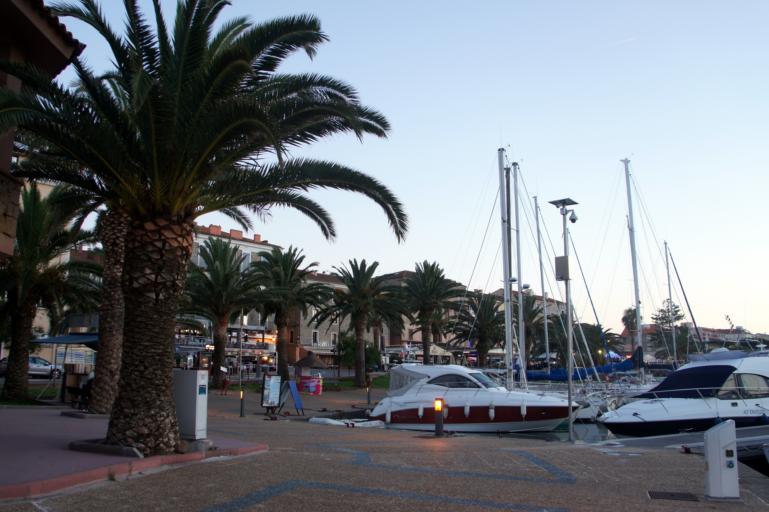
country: FR
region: Corsica
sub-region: Departement de la Corse-du-Sud
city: Propriano
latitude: 41.6762
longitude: 8.9034
